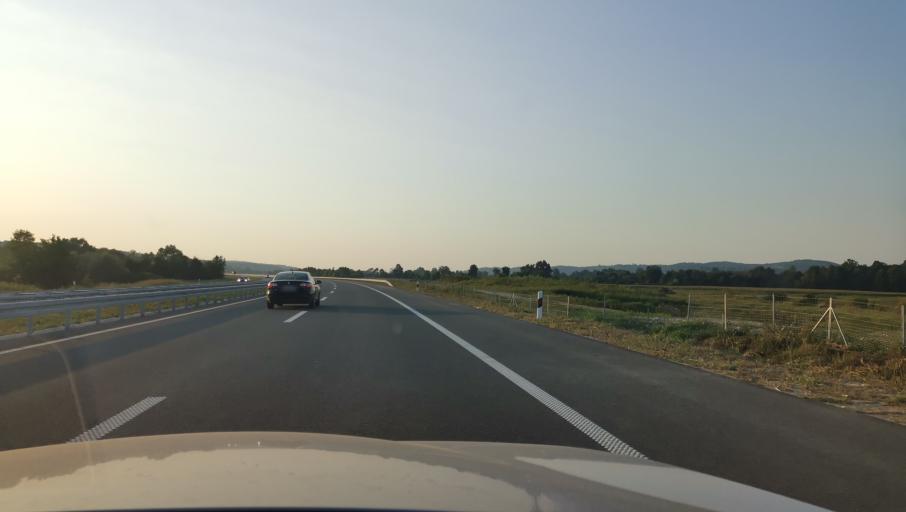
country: RS
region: Central Serbia
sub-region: Kolubarski Okrug
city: Ljig
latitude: 44.3048
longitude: 20.2299
